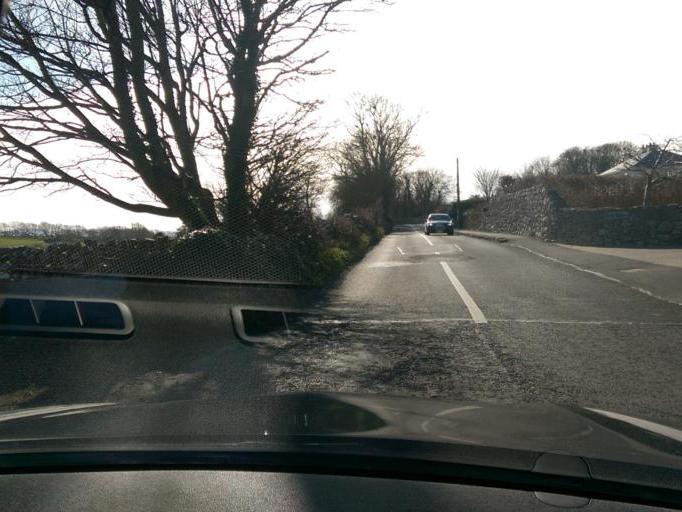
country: IE
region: Connaught
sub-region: County Galway
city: Oranmore
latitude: 53.2469
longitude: -8.9515
